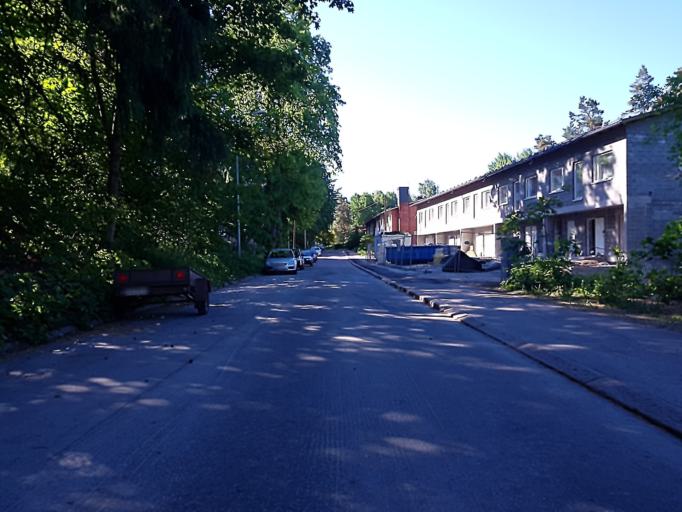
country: FI
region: Uusimaa
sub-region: Helsinki
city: Helsinki
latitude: 60.2259
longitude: 24.9241
